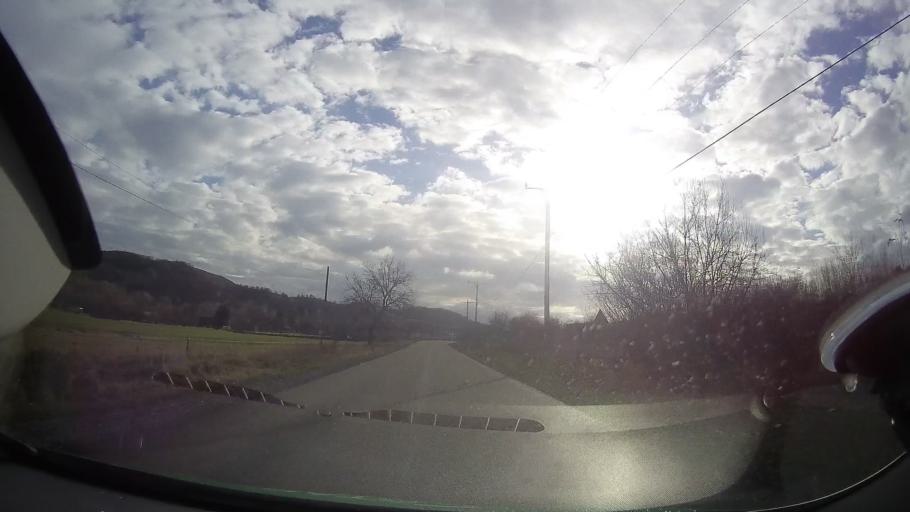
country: RO
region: Cluj
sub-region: Comuna Floresti
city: Luna de Sus
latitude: 46.7188
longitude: 23.4245
